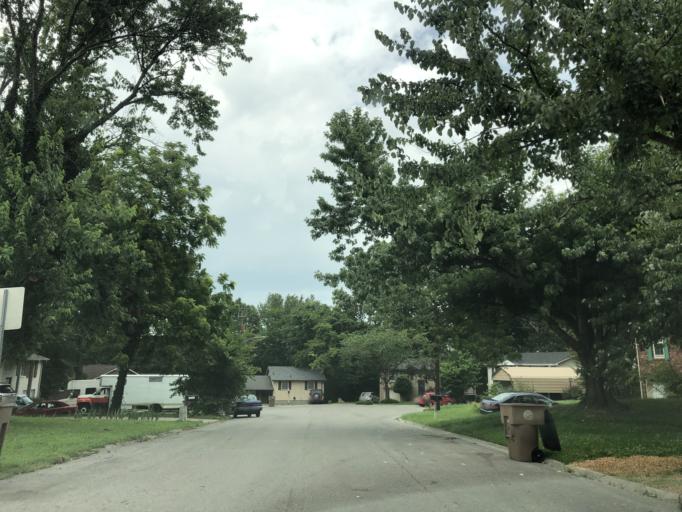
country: US
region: Tennessee
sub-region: Williamson County
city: Brentwood Estates
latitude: 36.0588
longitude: -86.6866
